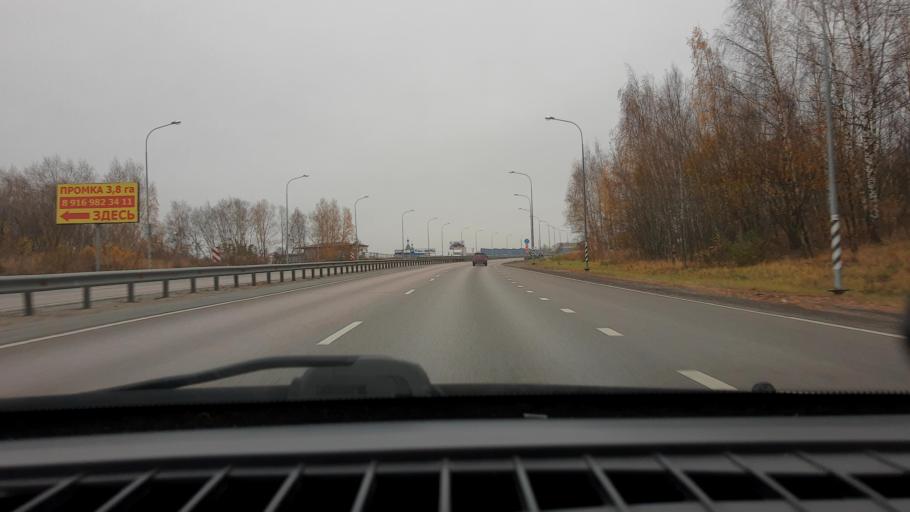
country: RU
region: Nizjnij Novgorod
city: Afonino
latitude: 56.2320
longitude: 44.0678
